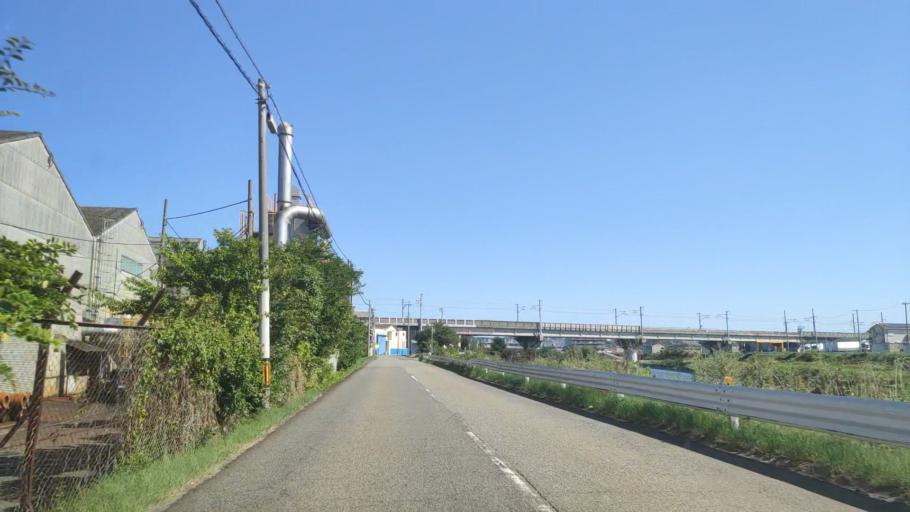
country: JP
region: Hyogo
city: Akashi
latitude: 34.6636
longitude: 134.9840
